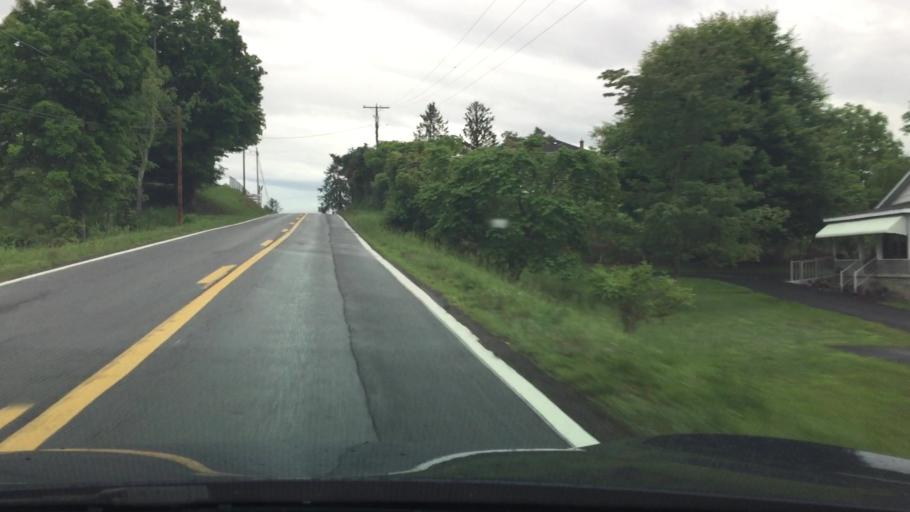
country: US
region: West Virginia
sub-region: Summers County
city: Hinton
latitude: 37.5714
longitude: -80.7890
